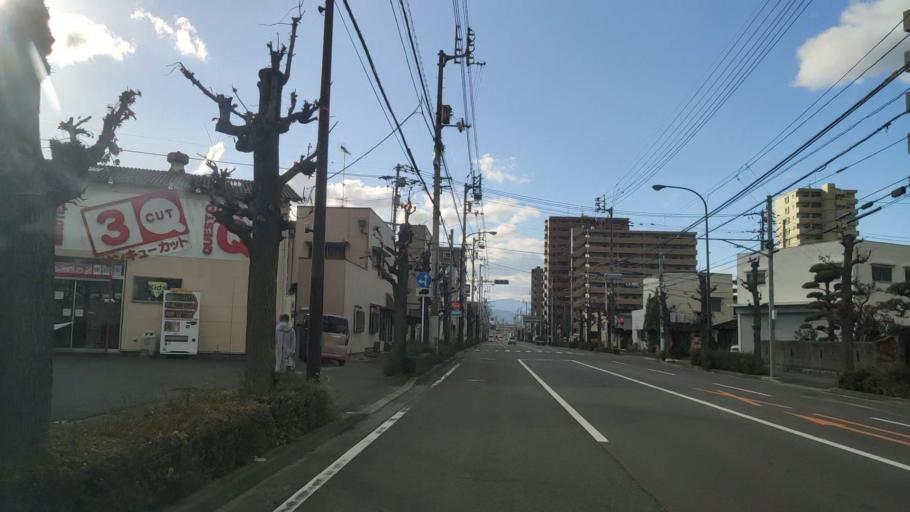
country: JP
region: Ehime
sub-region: Shikoku-chuo Shi
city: Matsuyama
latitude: 33.8338
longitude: 132.7525
